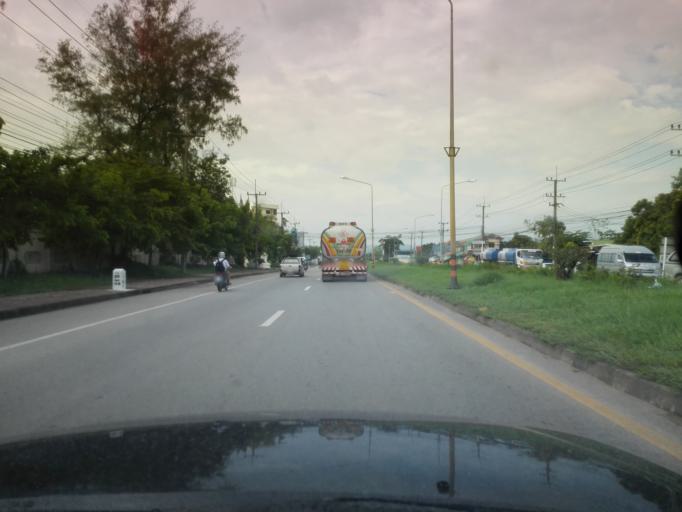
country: TH
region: Tak
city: Mae Sot
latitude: 16.7145
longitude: 98.5560
